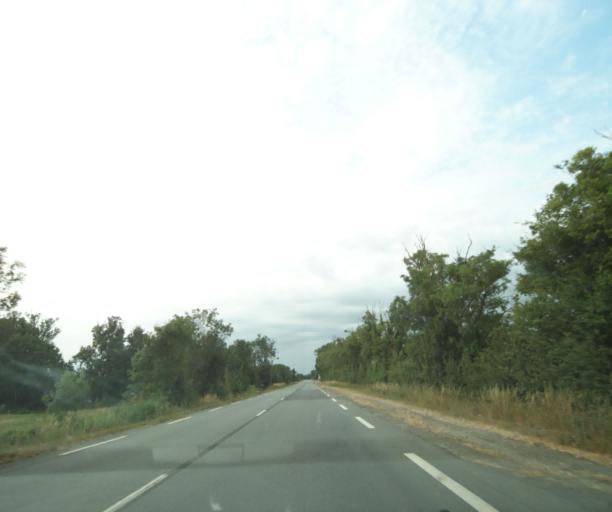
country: FR
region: Poitou-Charentes
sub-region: Departement de la Charente-Maritime
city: Marans
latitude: 46.3332
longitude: -0.9967
